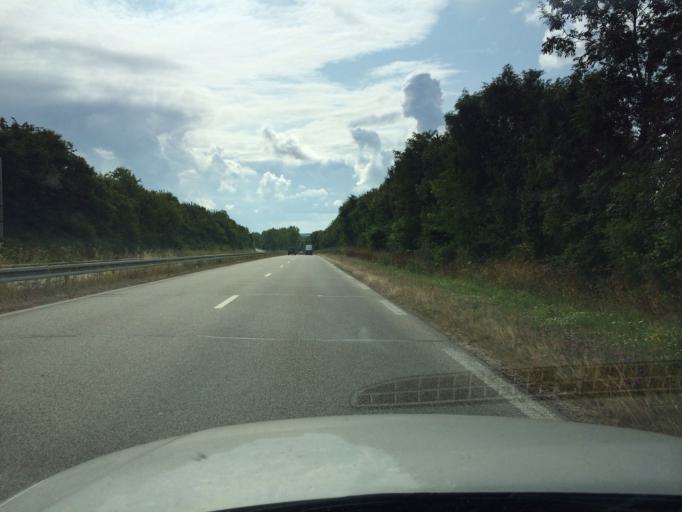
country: FR
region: Lower Normandy
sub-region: Departement de la Manche
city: Montebourg
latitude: 49.4854
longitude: -1.3958
